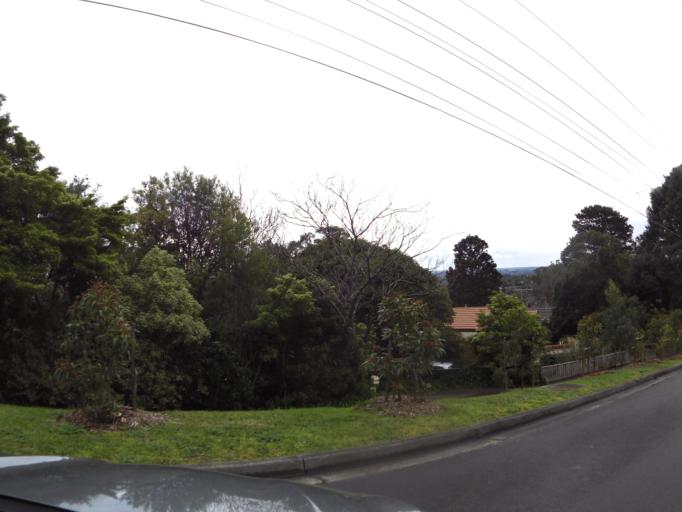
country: AU
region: Victoria
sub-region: Knox
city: Boronia
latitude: -37.8669
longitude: 145.3007
